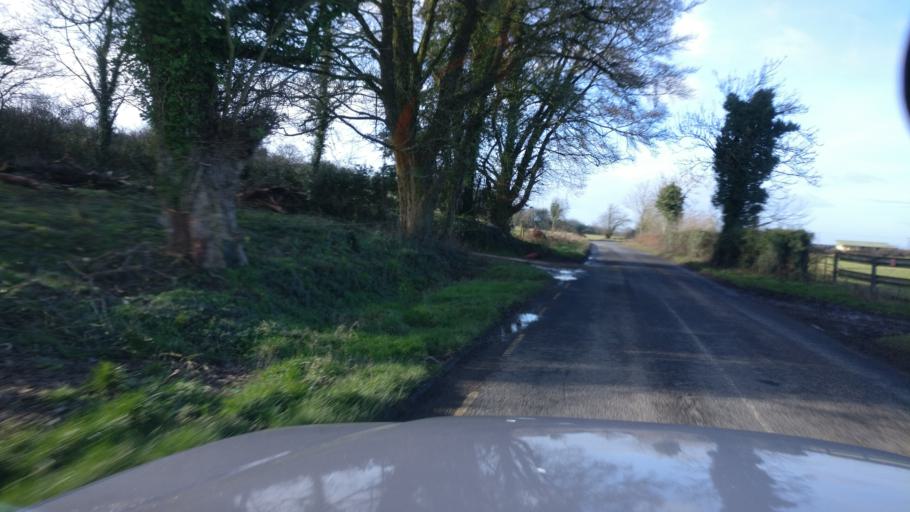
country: IE
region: Leinster
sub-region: Laois
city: Portlaoise
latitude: 53.0089
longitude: -7.2359
